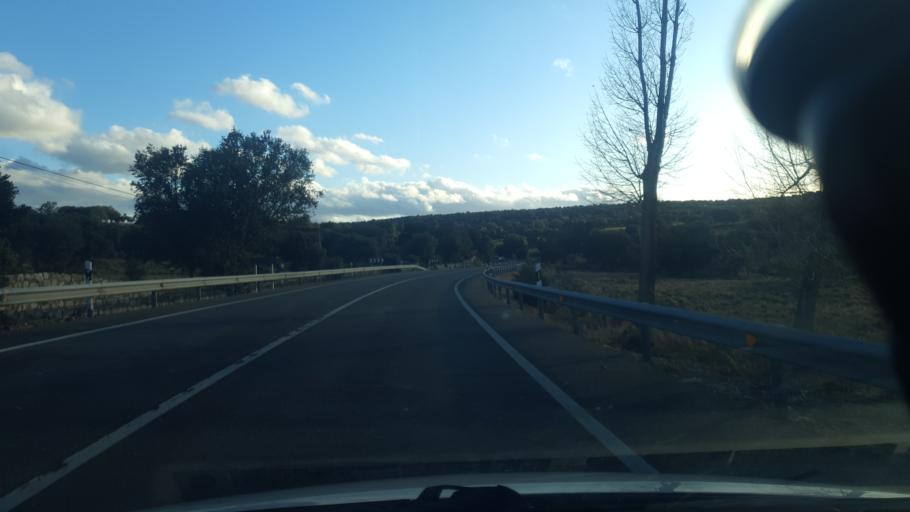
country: ES
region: Castille and Leon
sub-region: Provincia de Avila
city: Mingorria
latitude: 40.7329
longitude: -4.6751
